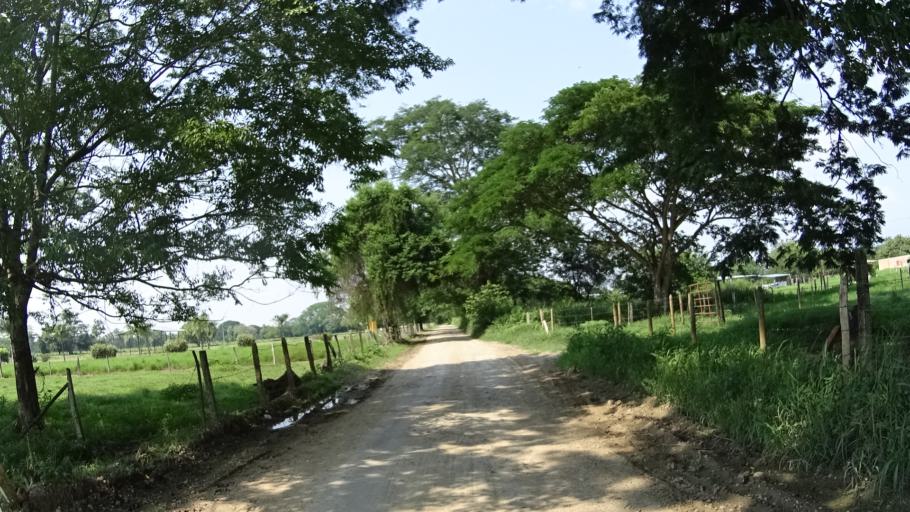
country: CO
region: Cundinamarca
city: Puerto Salgar
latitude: 5.5253
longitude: -74.6863
